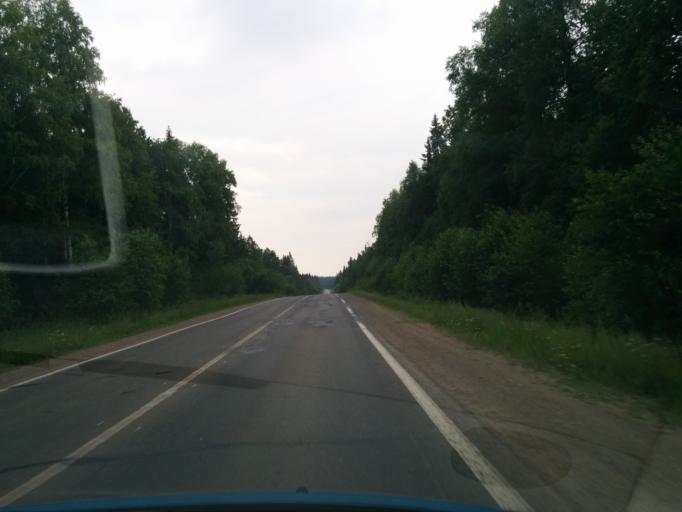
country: RU
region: Perm
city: Perm
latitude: 58.1870
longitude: 56.2188
